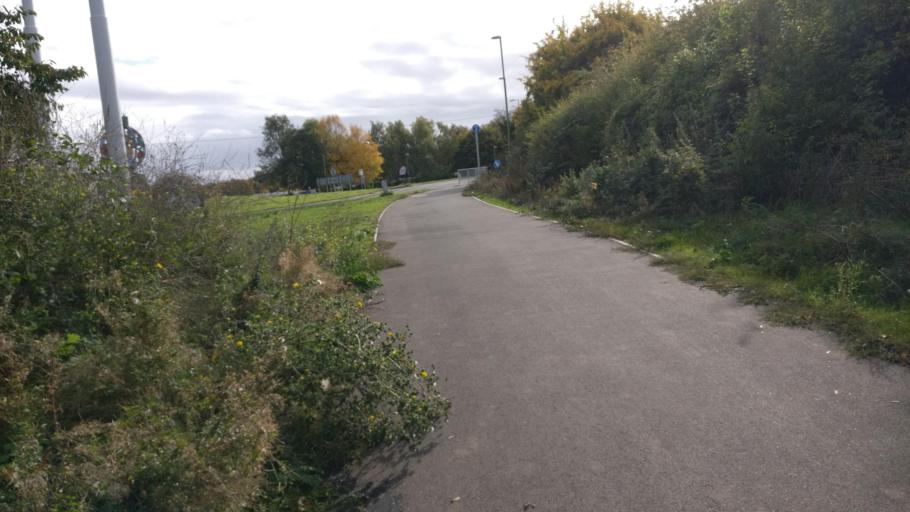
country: GB
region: England
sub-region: Hampshire
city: Basingstoke
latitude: 51.2361
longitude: -1.1413
